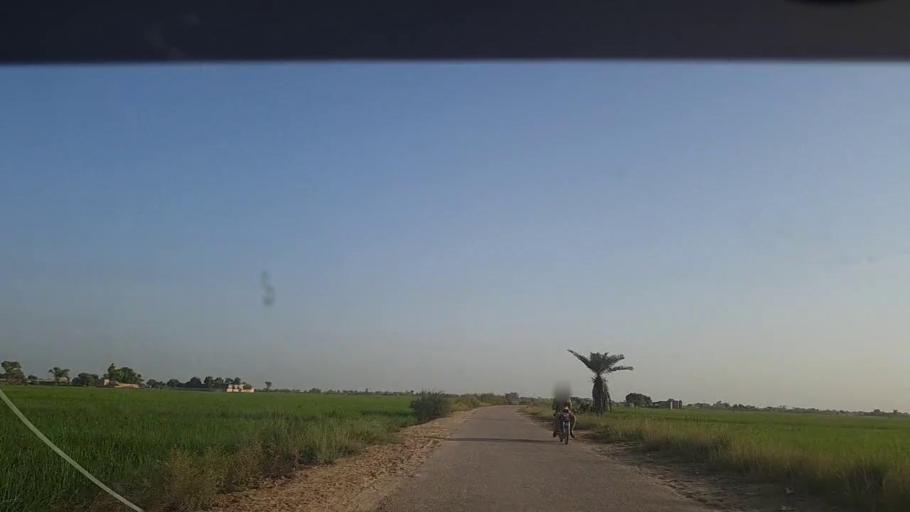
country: PK
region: Sindh
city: Thul
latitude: 28.1990
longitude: 68.8740
